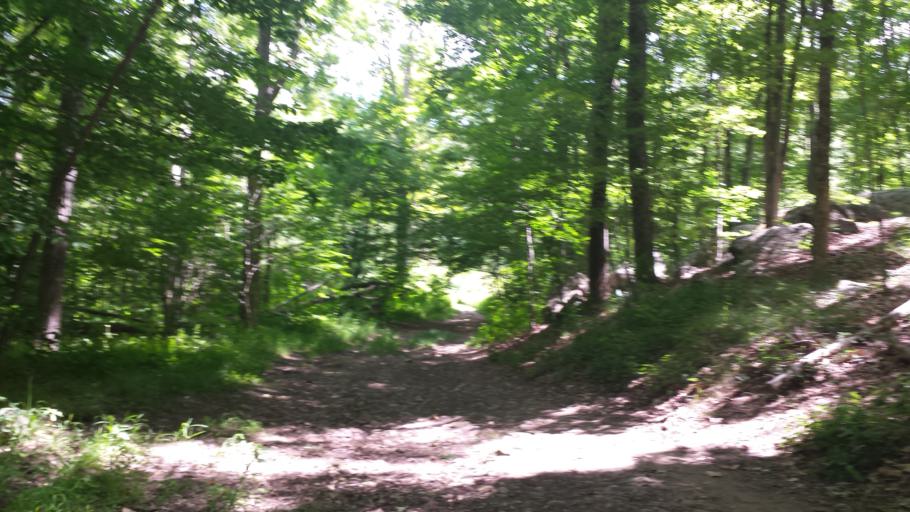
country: US
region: New York
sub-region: Westchester County
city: Pound Ridge
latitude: 41.2610
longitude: -73.5783
